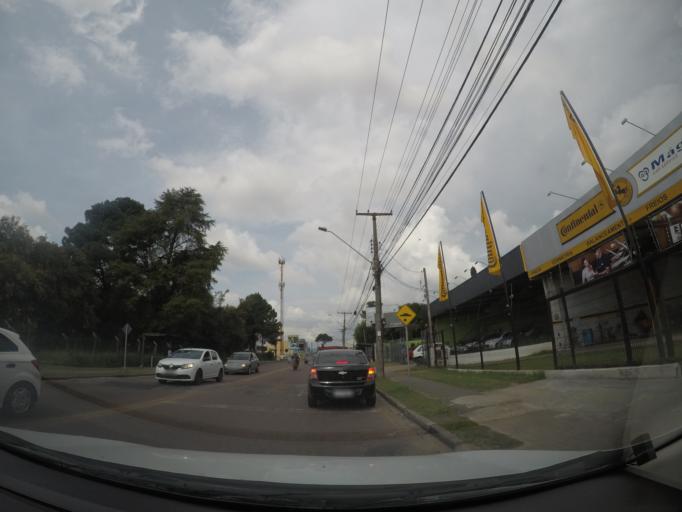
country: BR
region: Parana
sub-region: Sao Jose Dos Pinhais
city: Sao Jose dos Pinhais
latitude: -25.5013
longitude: -49.2662
